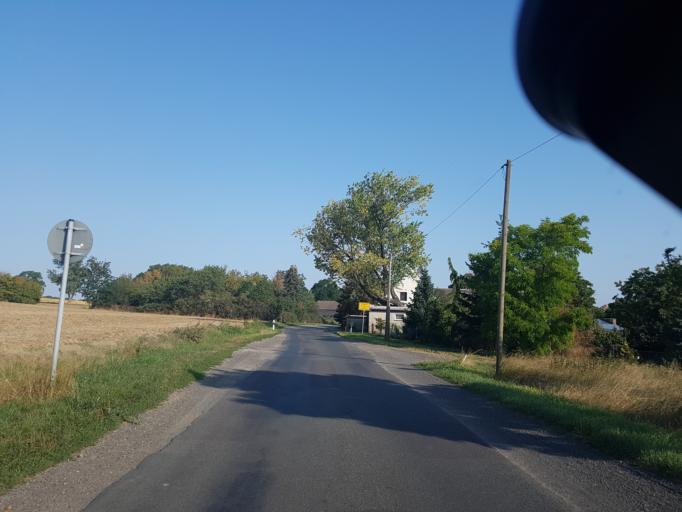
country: DE
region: Brandenburg
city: Niemegk
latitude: 52.0242
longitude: 12.6816
